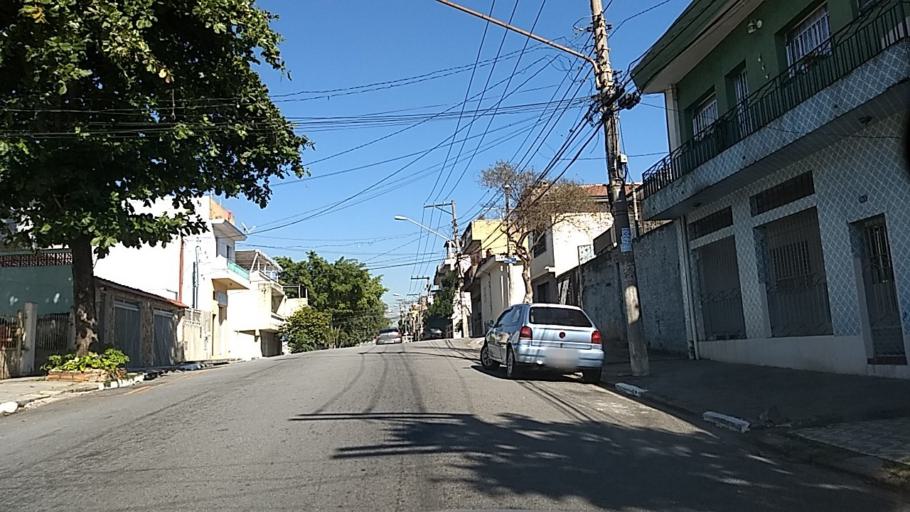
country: BR
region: Sao Paulo
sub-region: Guarulhos
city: Guarulhos
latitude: -23.4894
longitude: -46.5788
